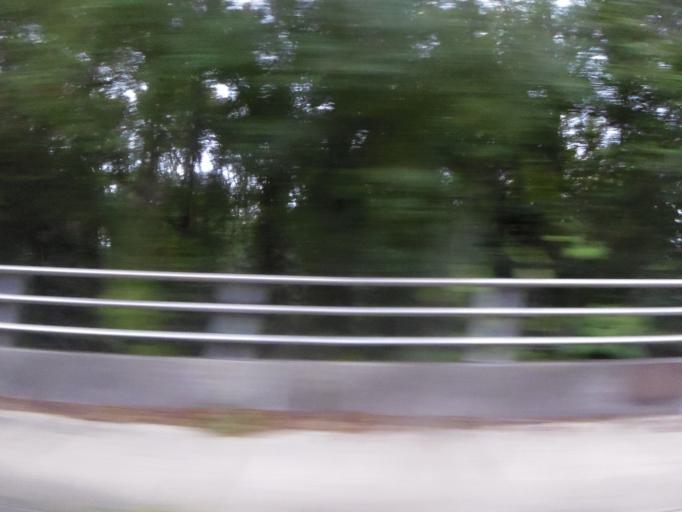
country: US
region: Florida
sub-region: Clay County
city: Bellair-Meadowbrook Terrace
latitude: 30.2704
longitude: -81.7435
